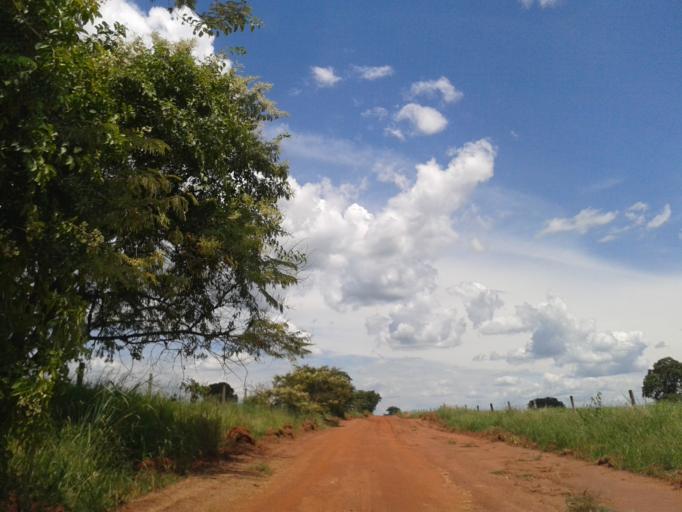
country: BR
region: Minas Gerais
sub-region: Ituiutaba
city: Ituiutaba
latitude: -18.8758
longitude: -49.4803
